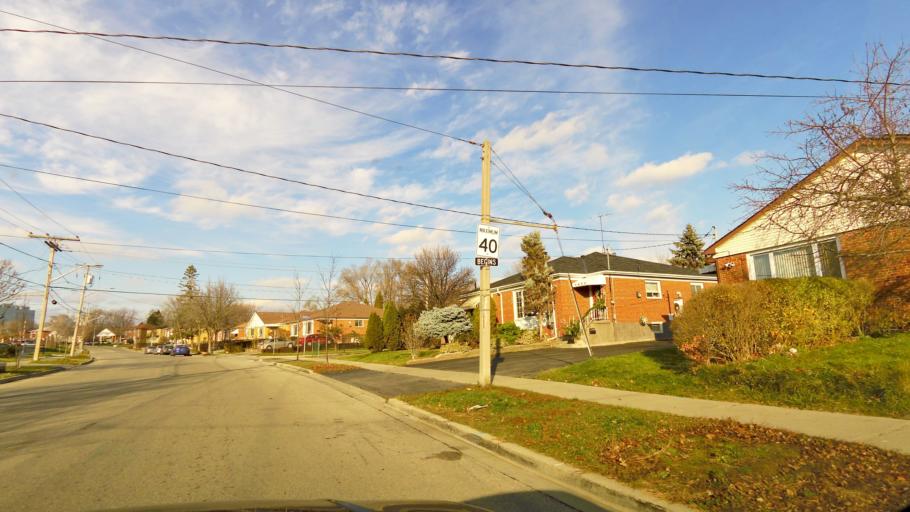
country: CA
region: Ontario
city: Mississauga
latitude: 43.5603
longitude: -79.6611
